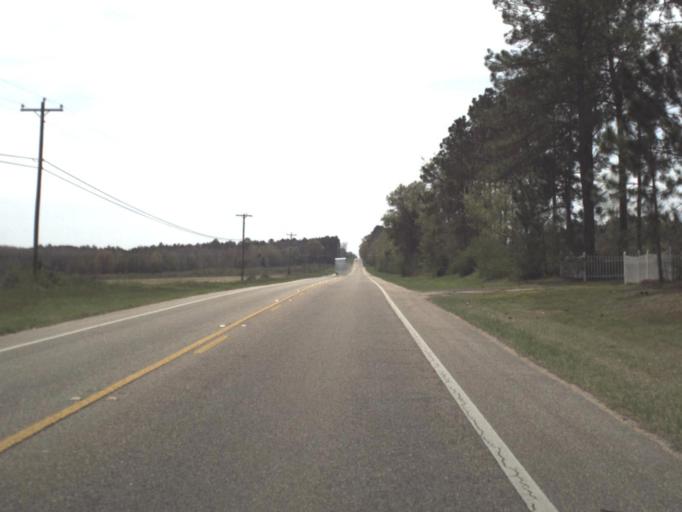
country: US
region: Florida
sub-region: Jackson County
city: Graceville
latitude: 30.9097
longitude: -85.5217
